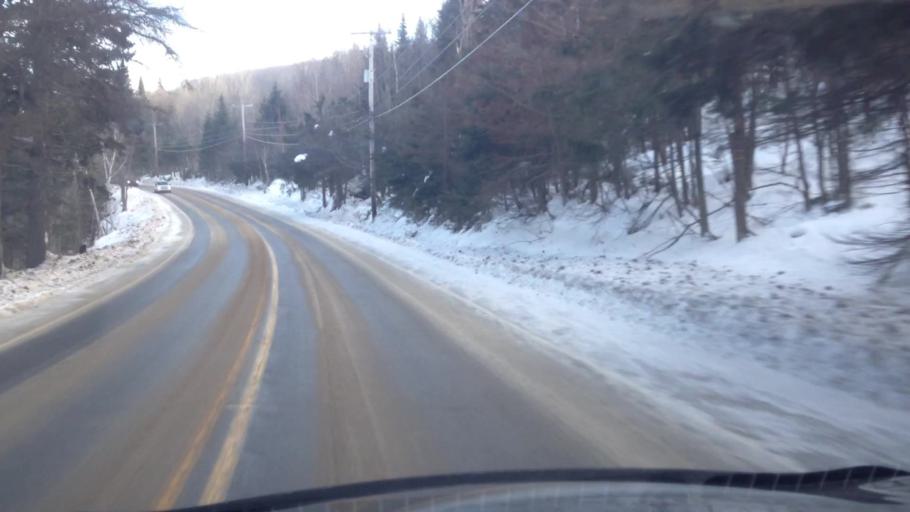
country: CA
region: Quebec
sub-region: Laurentides
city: Sainte-Agathe-des-Monts
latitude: 45.9160
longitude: -74.3724
